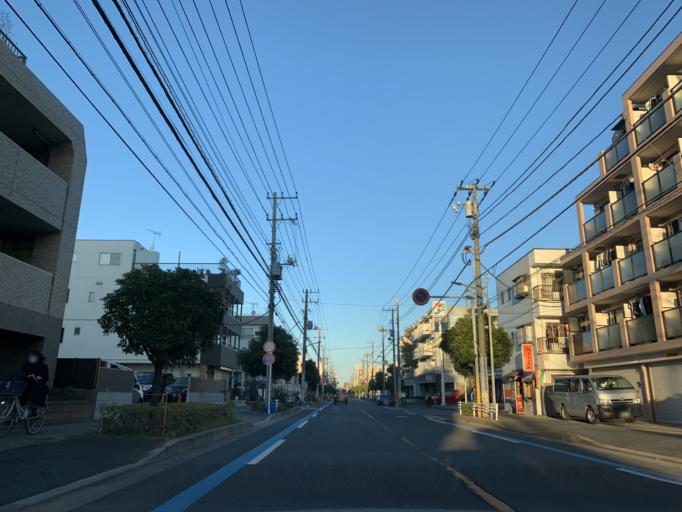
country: JP
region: Tokyo
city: Urayasu
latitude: 35.6803
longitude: 139.9215
